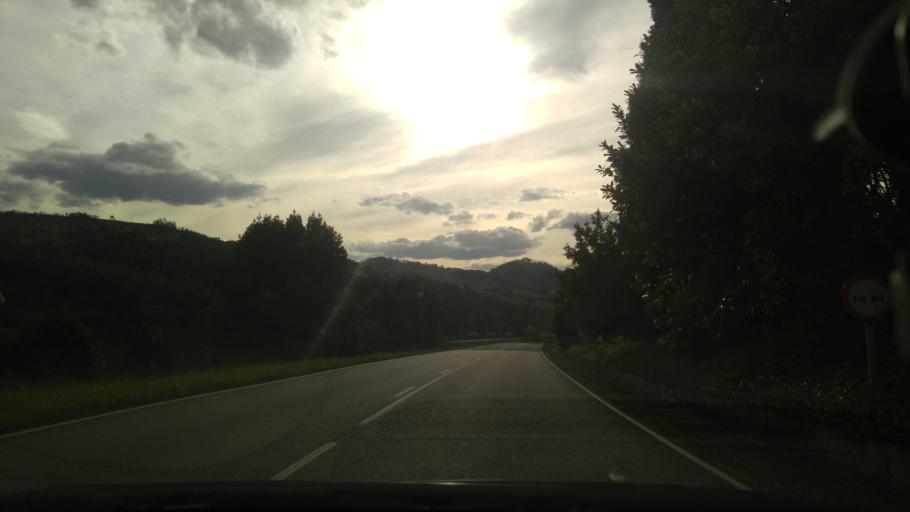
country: ES
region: Asturias
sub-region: Province of Asturias
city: Corvera de Asturias
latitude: 43.4768
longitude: -5.8488
